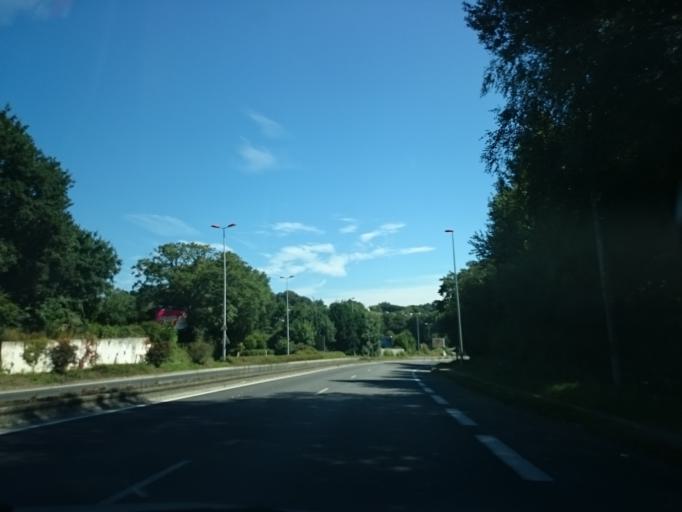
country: FR
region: Brittany
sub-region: Departement du Finistere
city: Bohars
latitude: 48.4107
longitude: -4.5315
